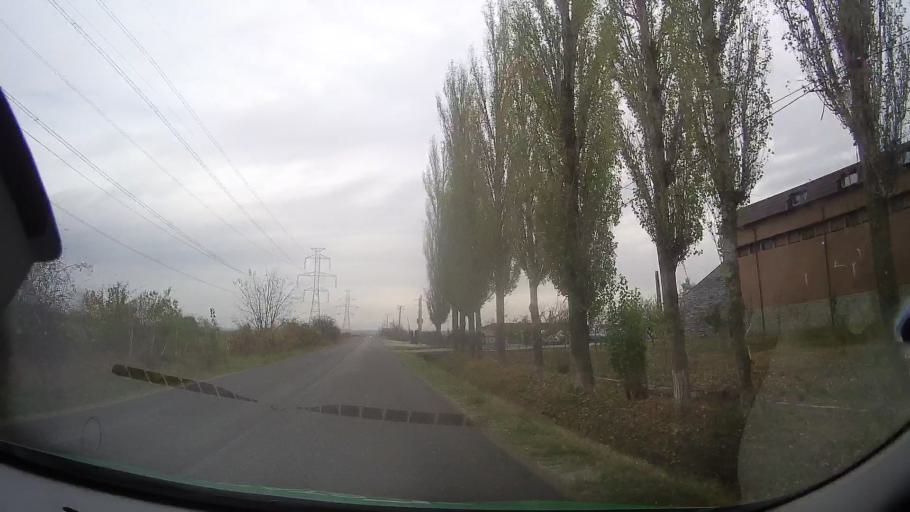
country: RO
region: Prahova
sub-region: Comuna Valea Calugareasca
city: Pantazi
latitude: 44.9291
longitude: 26.1473
